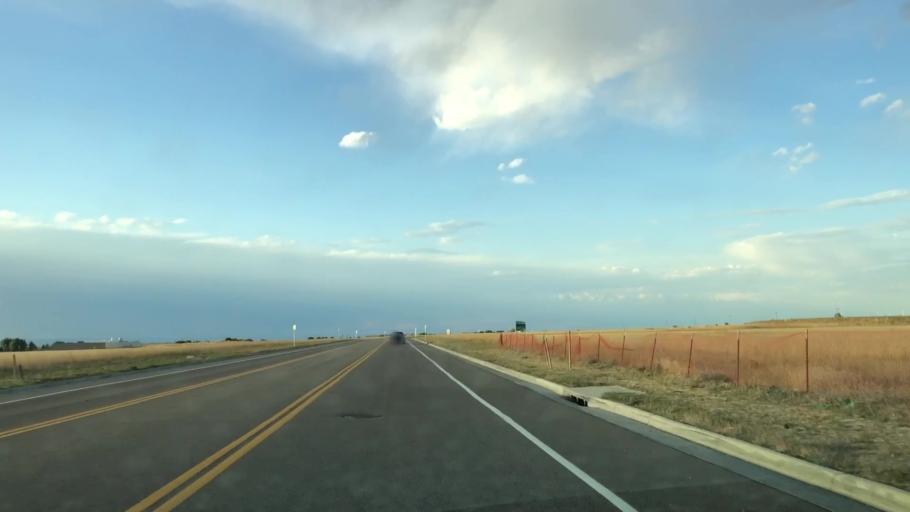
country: US
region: Colorado
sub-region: Larimer County
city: Loveland
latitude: 40.4395
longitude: -104.9960
